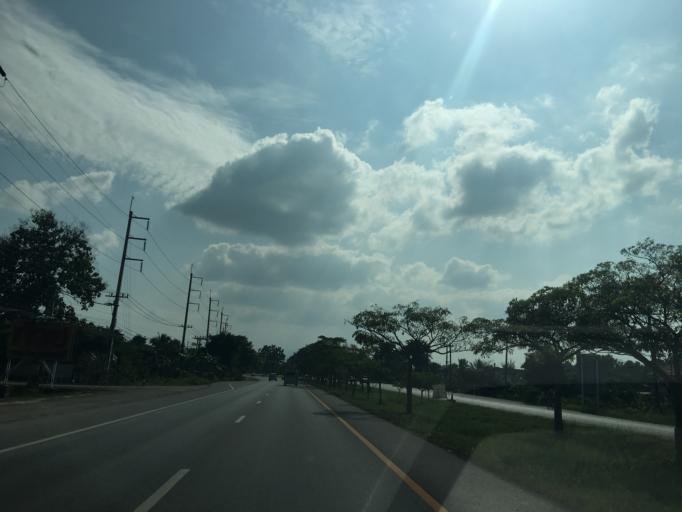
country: TH
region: Chiang Rai
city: Mae Lao
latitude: 19.7294
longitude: 99.7178
